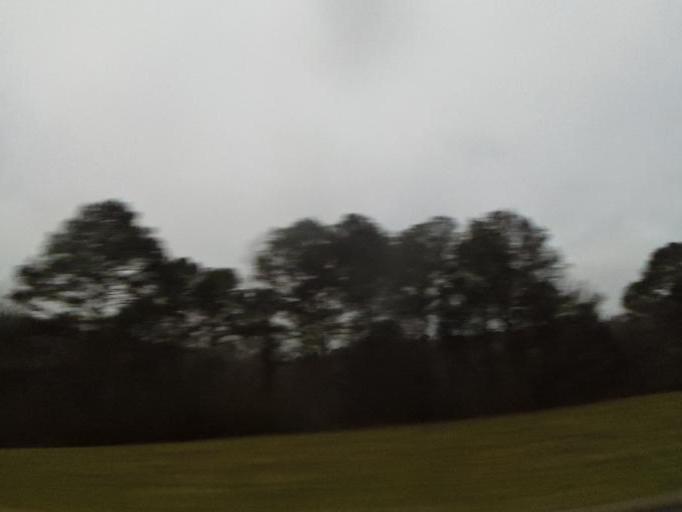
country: US
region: Alabama
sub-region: Cullman County
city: Cullman
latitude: 34.2289
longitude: -86.8785
